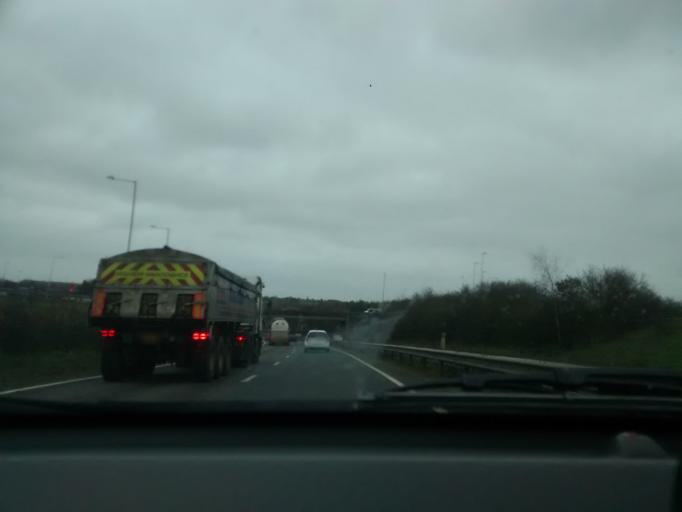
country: GB
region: England
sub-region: Suffolk
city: Bramford
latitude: 52.0380
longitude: 1.0969
